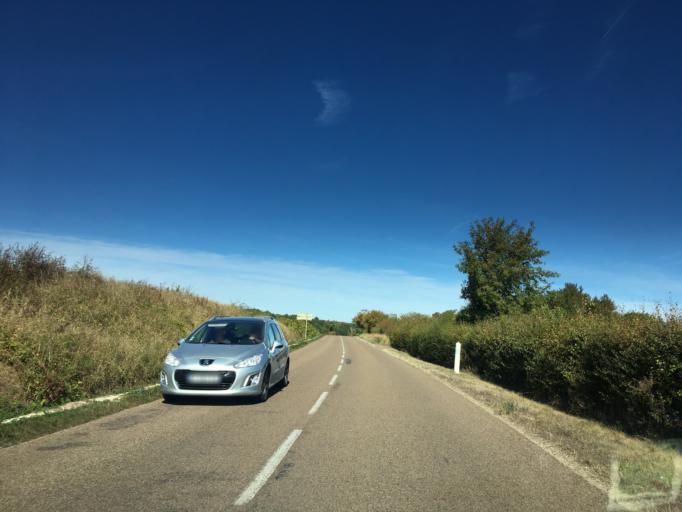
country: FR
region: Bourgogne
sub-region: Departement de l'Yonne
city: Vermenton
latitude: 47.6114
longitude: 3.6777
